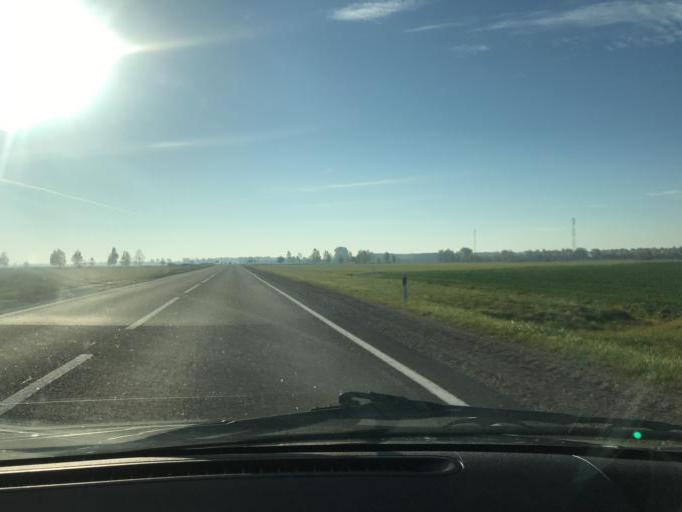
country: BY
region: Brest
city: Drahichyn
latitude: 52.1681
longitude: 25.3198
